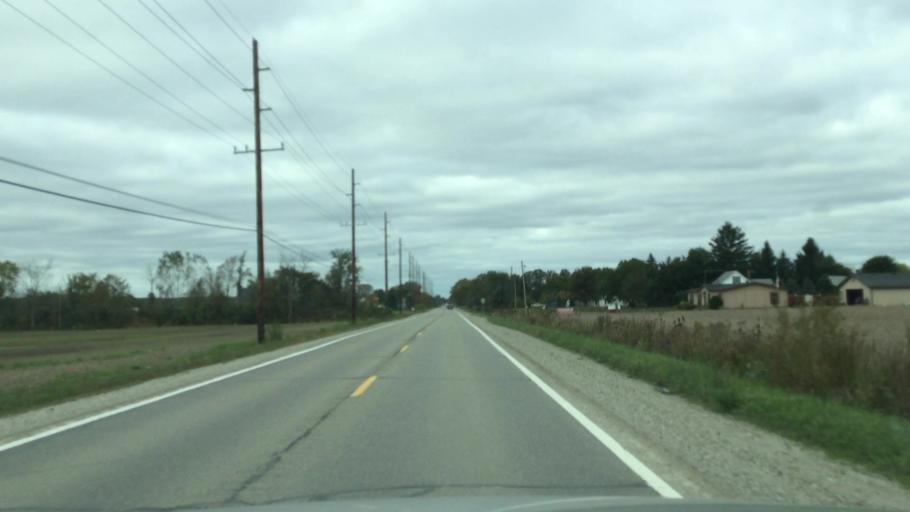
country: US
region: Michigan
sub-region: Macomb County
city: Richmond
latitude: 42.8080
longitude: -82.8124
